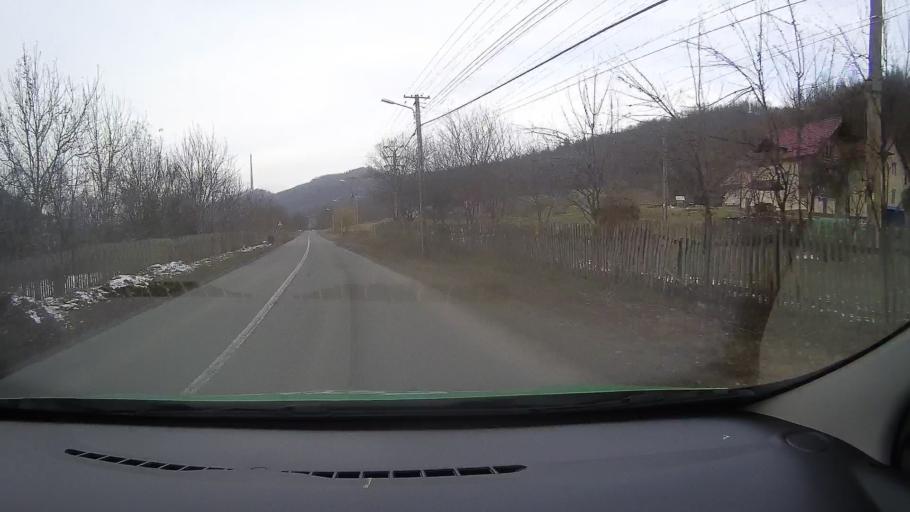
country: RO
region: Alba
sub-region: Oras Zlatna
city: Zlatna
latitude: 46.0950
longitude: 23.2555
